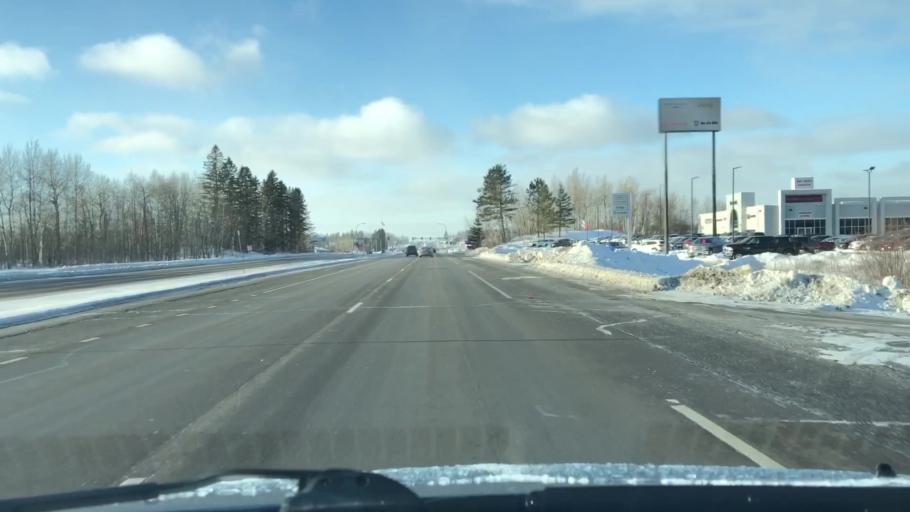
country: US
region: Minnesota
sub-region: Saint Louis County
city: Hermantown
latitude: 46.8171
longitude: -92.1784
